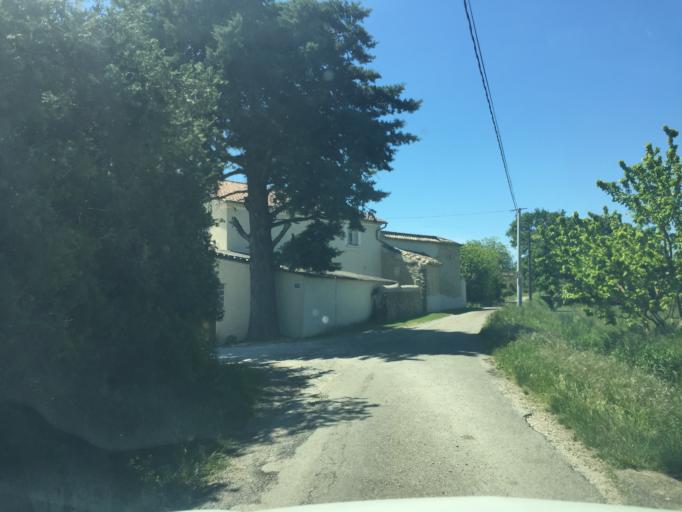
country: FR
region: Provence-Alpes-Cote d'Azur
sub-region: Departement du Vaucluse
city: Orange
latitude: 44.1164
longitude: 4.7912
